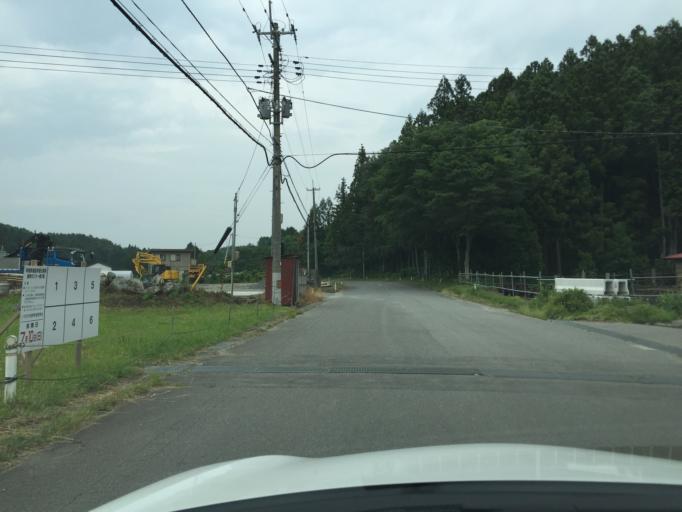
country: JP
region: Fukushima
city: Iwaki
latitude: 37.1976
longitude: 140.7207
